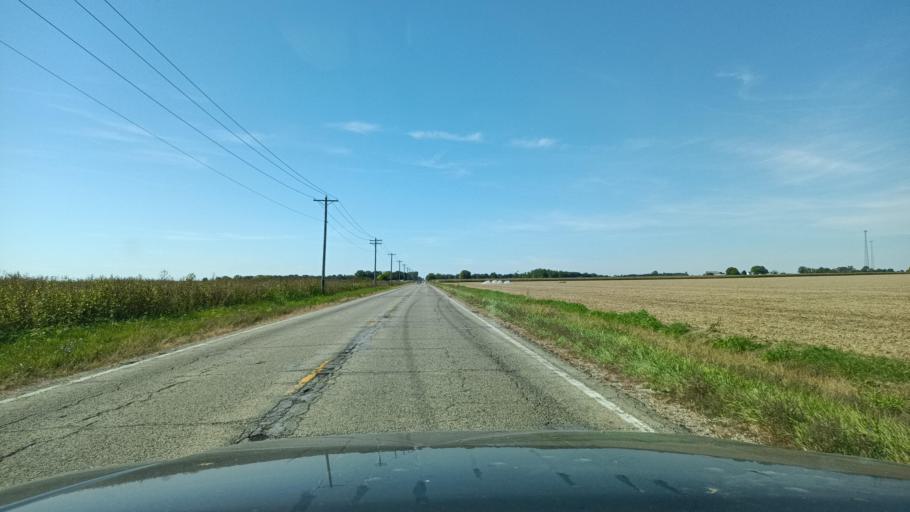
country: US
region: Illinois
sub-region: Champaign County
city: Mahomet
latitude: 40.2066
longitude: -88.4761
